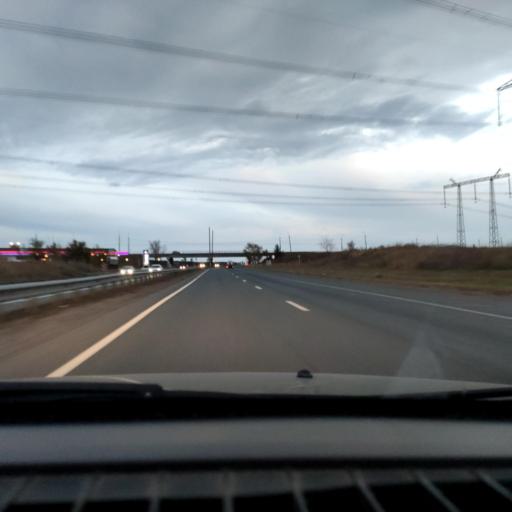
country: RU
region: Samara
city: Zhigulevsk
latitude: 53.5197
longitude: 49.5323
